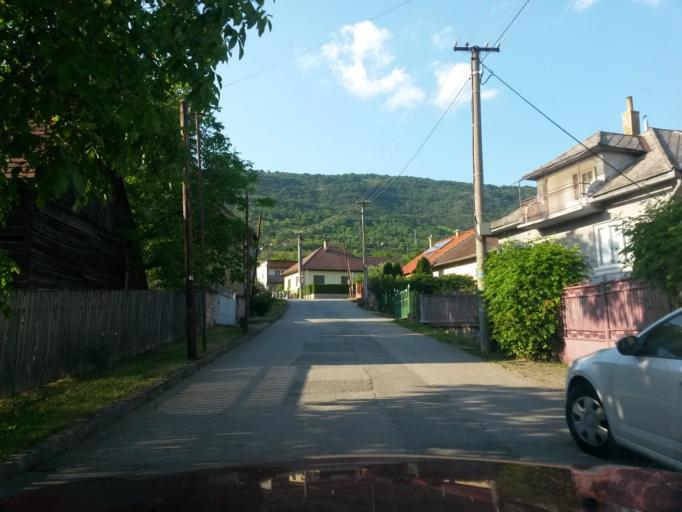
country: SK
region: Kosicky
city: Roznava
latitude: 48.5929
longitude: 20.6745
